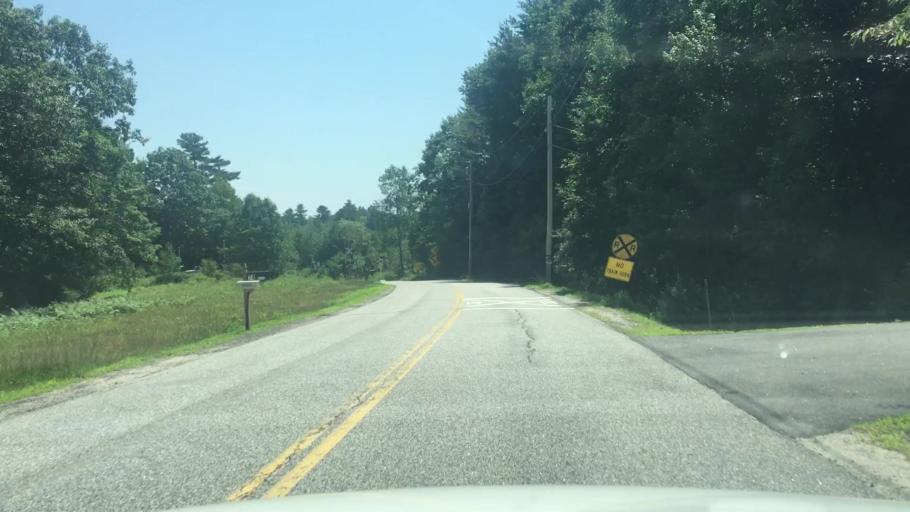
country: US
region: Maine
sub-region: Cumberland County
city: Falmouth
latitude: 43.7524
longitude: -70.2753
